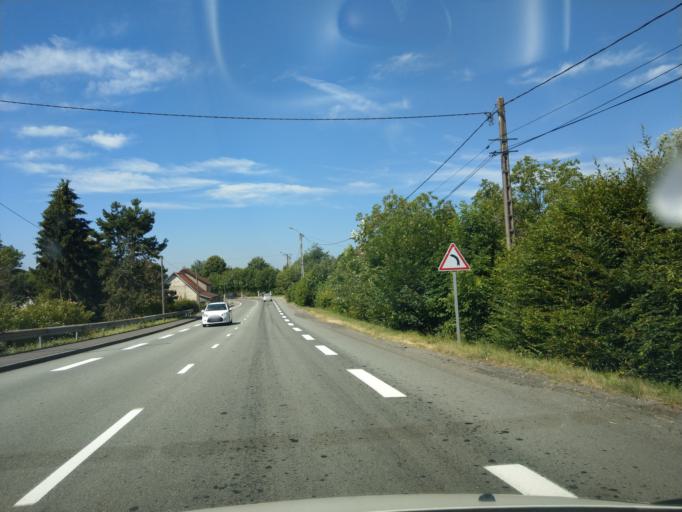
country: FR
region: Franche-Comte
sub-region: Territoire de Belfort
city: Chevremont
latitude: 47.6735
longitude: 6.9261
